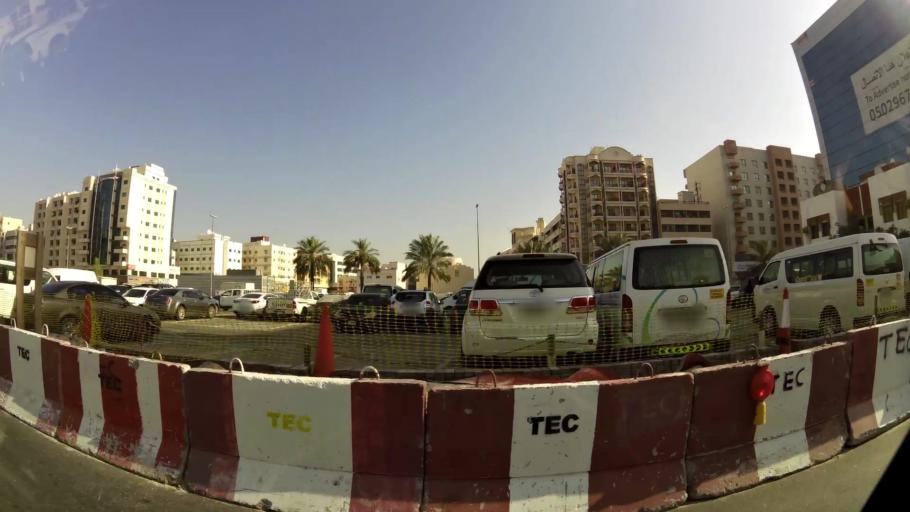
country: AE
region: Ash Shariqah
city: Sharjah
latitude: 25.2590
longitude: 55.2930
